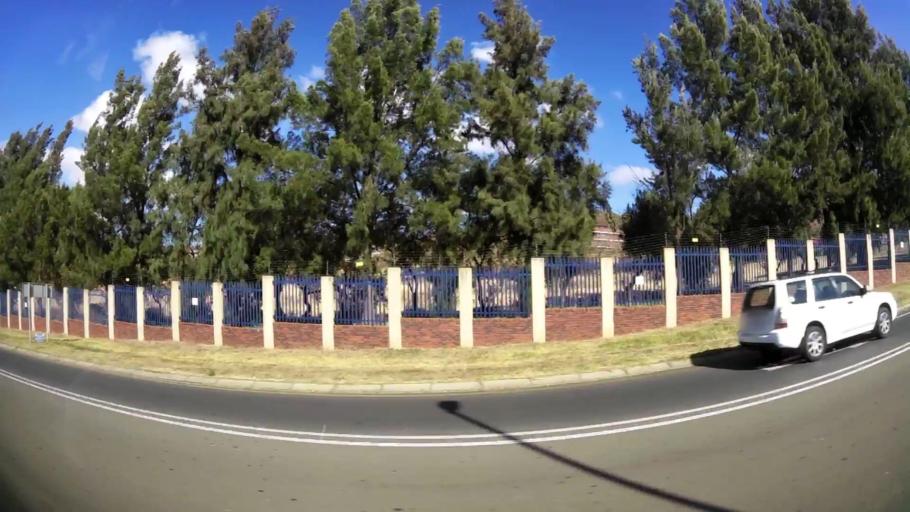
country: ZA
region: Gauteng
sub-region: West Rand District Municipality
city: Krugersdorp
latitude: -26.1025
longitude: 27.8373
